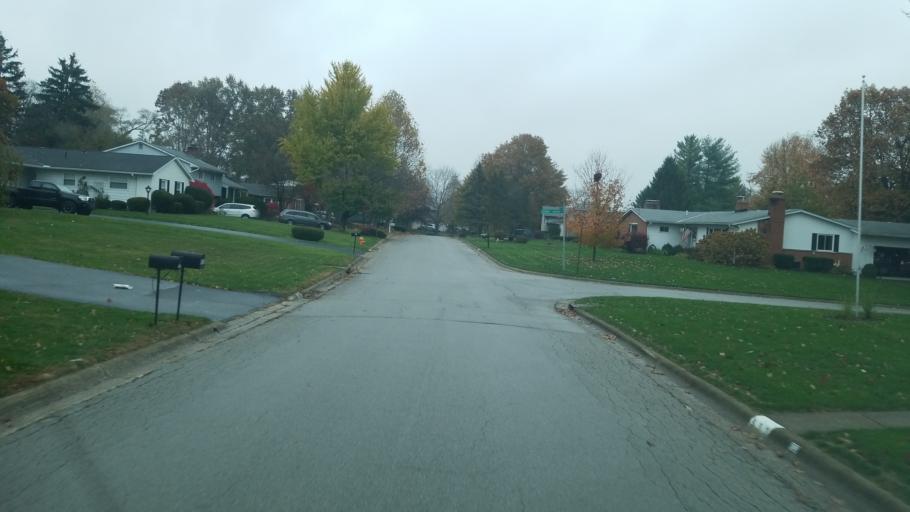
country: US
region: Ohio
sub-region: Franklin County
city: Worthington
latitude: 40.0793
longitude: -83.0434
